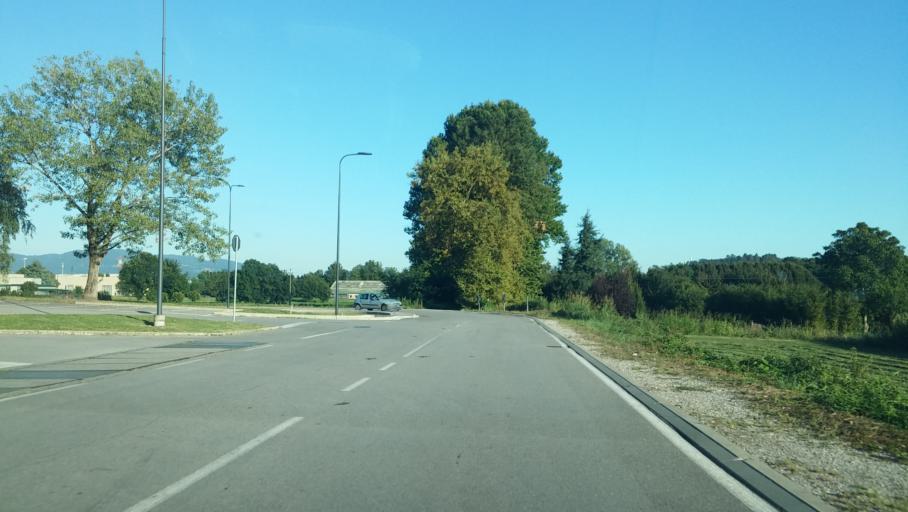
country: IT
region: Lombardy
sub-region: Provincia di Como
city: Erba
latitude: 45.8014
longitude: 9.2203
